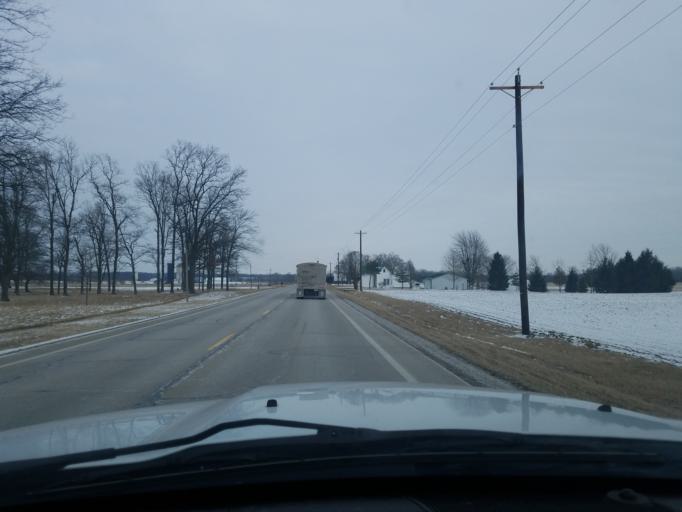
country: US
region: Indiana
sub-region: Randolph County
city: Lynn
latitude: 40.0487
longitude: -84.9795
